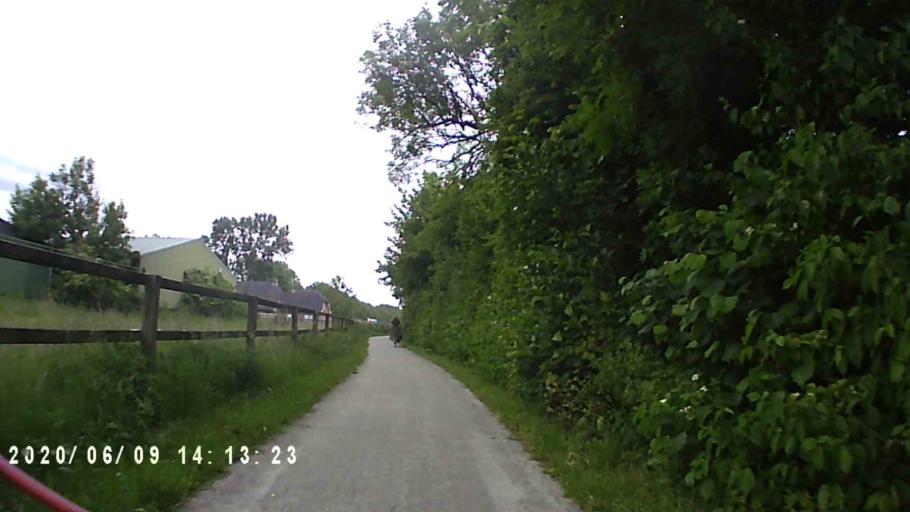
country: NL
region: Groningen
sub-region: Gemeente Bedum
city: Bedum
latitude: 53.2768
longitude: 6.6034
